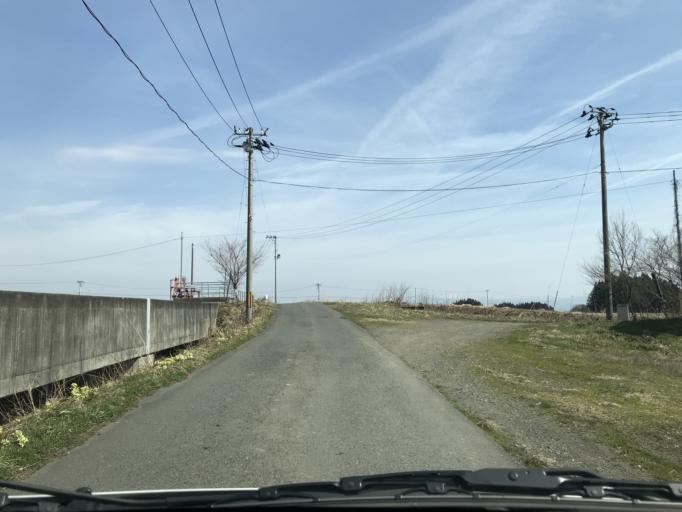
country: JP
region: Iwate
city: Mizusawa
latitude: 39.1057
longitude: 141.0108
